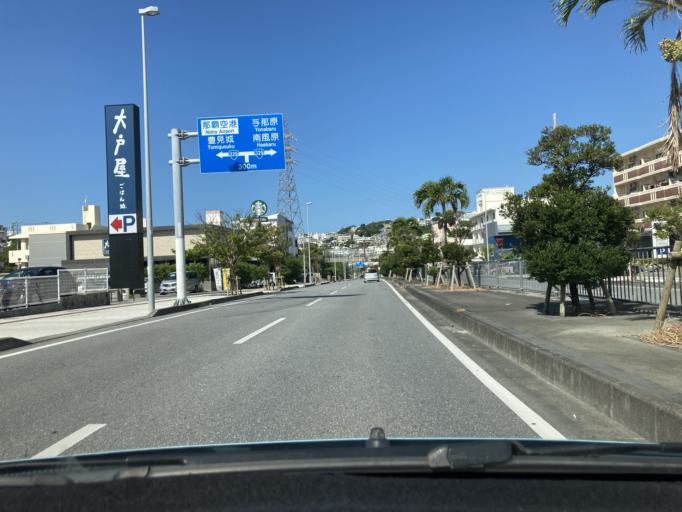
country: JP
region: Okinawa
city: Tomigusuku
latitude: 26.1934
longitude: 127.7130
